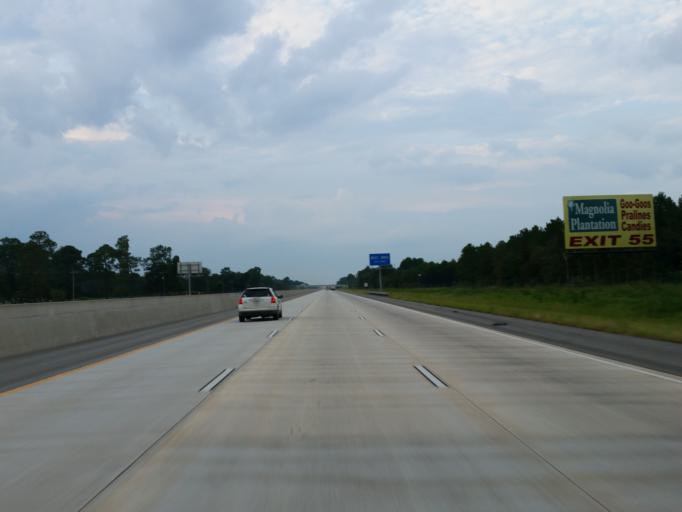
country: US
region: Georgia
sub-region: Cook County
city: Sparks
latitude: 31.2243
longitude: -83.4618
